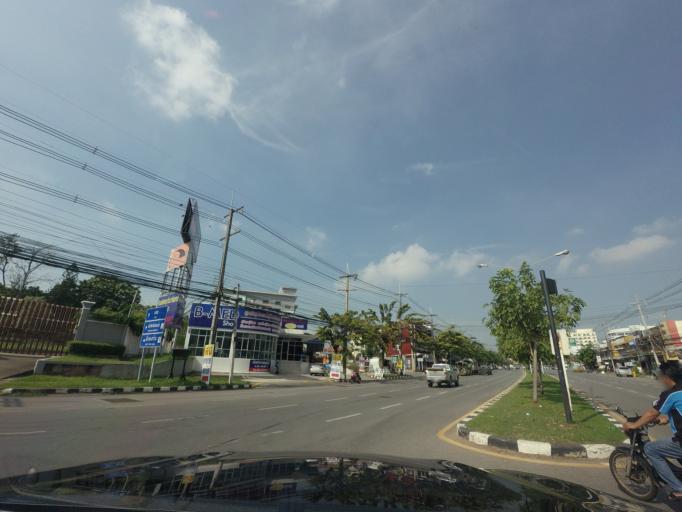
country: TH
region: Khon Kaen
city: Khon Kaen
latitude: 16.4286
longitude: 102.8541
